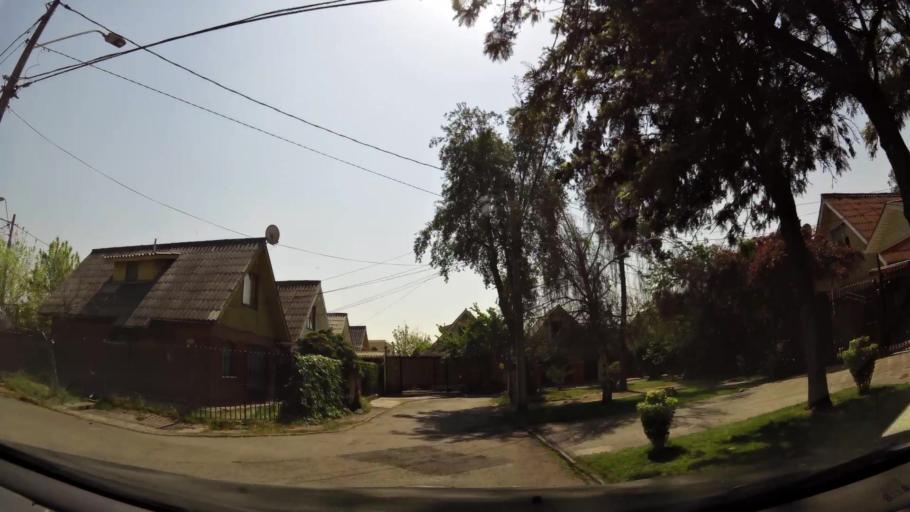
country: CL
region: Santiago Metropolitan
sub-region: Provincia de Maipo
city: San Bernardo
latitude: -33.5869
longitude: -70.7103
